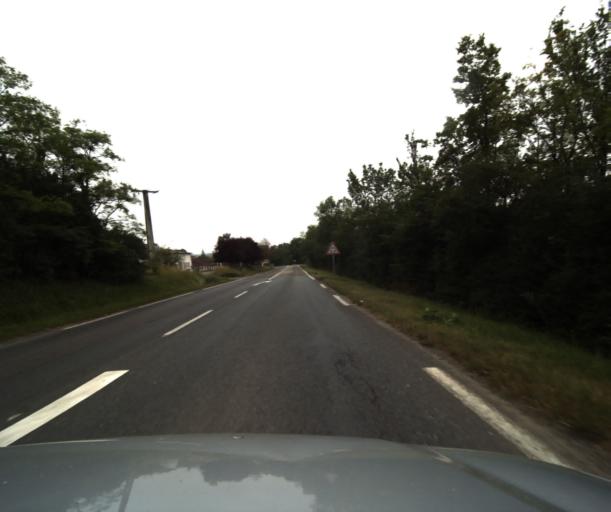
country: FR
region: Midi-Pyrenees
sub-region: Departement du Gers
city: Auch
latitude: 43.6529
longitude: 0.6143
